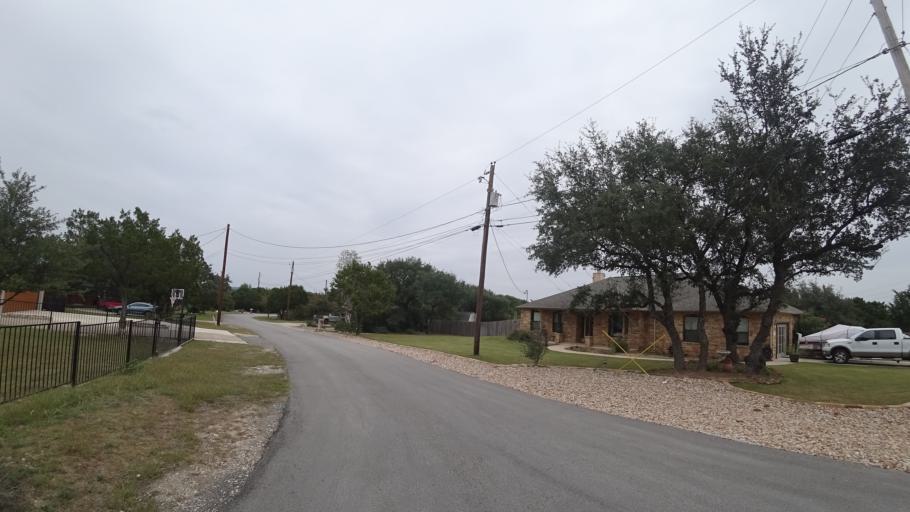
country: US
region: Texas
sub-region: Travis County
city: Hudson Bend
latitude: 30.3696
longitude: -97.9294
